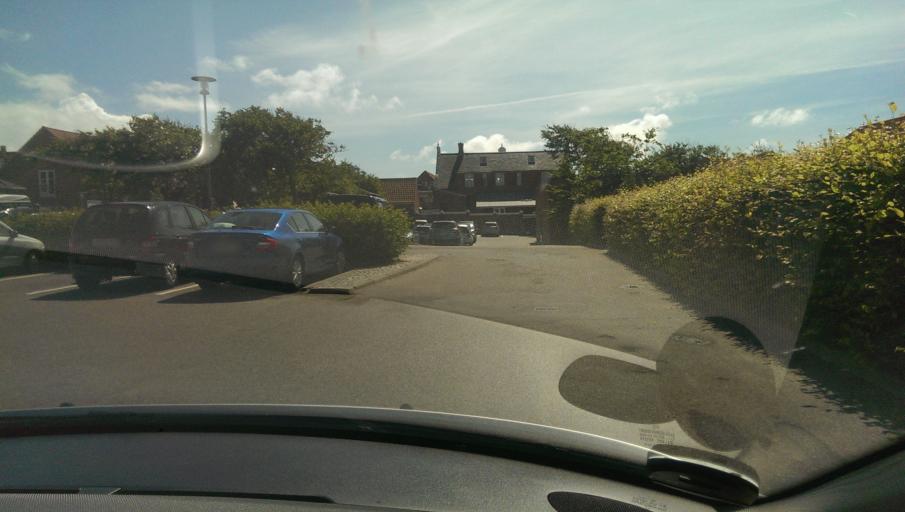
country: DK
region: Central Jutland
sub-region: Ringkobing-Skjern Kommune
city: Ringkobing
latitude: 56.0916
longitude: 8.2430
